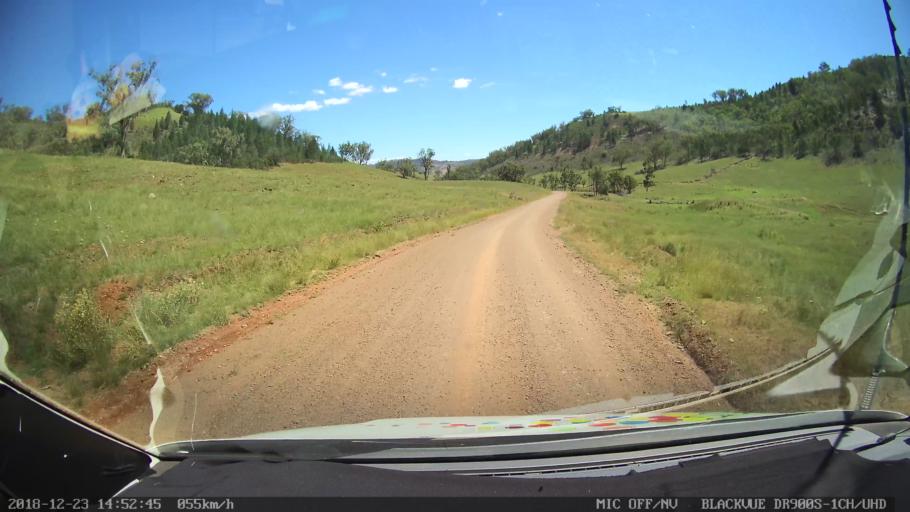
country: AU
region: New South Wales
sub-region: Tamworth Municipality
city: Manilla
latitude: -30.6863
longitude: 150.8537
